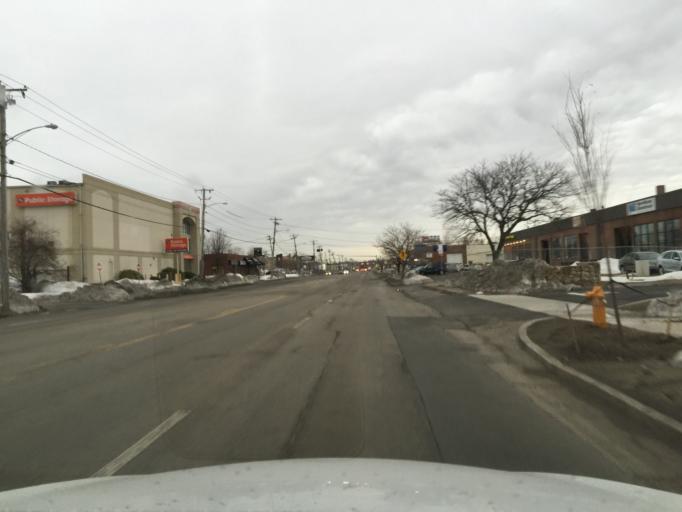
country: US
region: Massachusetts
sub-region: Middlesex County
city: Somerville
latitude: 42.4034
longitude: -71.0992
